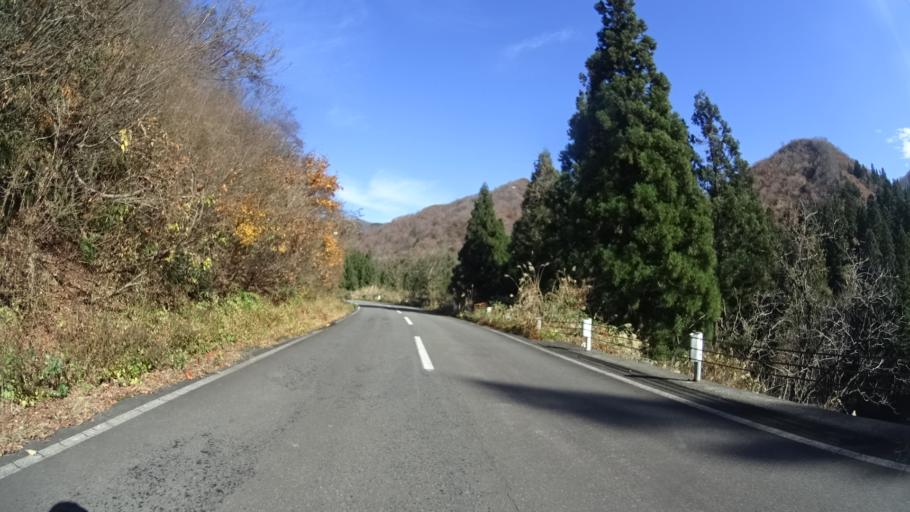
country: JP
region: Niigata
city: Muikamachi
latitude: 37.1839
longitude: 139.0804
